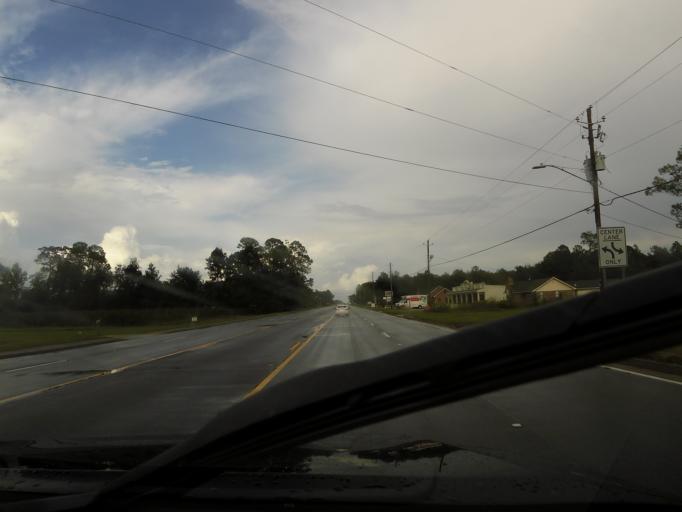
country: US
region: Georgia
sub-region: Long County
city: Ludowici
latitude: 31.7153
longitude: -81.7419
